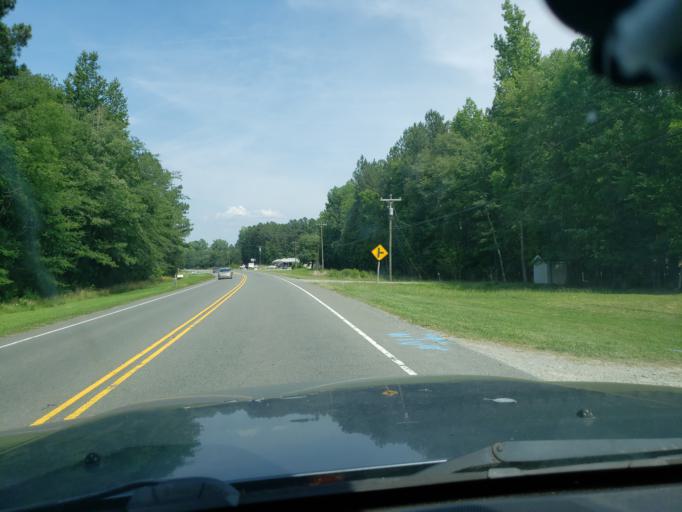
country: US
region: North Carolina
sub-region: Orange County
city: Carrboro
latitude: 35.9224
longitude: -79.1899
